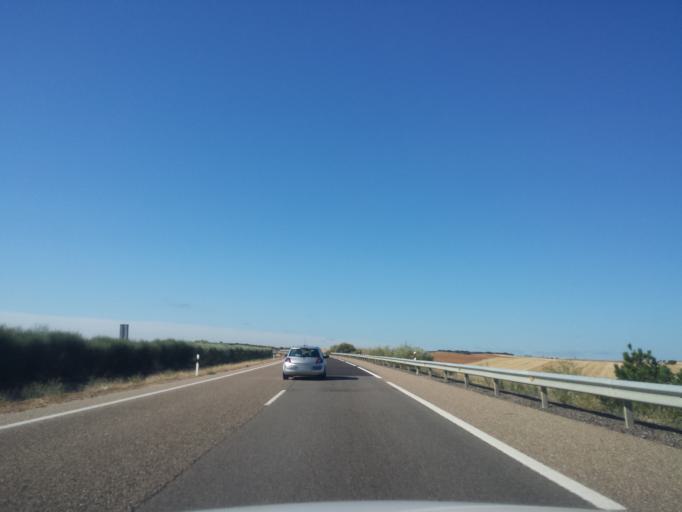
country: ES
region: Castille and Leon
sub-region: Provincia de Zamora
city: Matilla de Arzon
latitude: 42.1151
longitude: -5.6579
